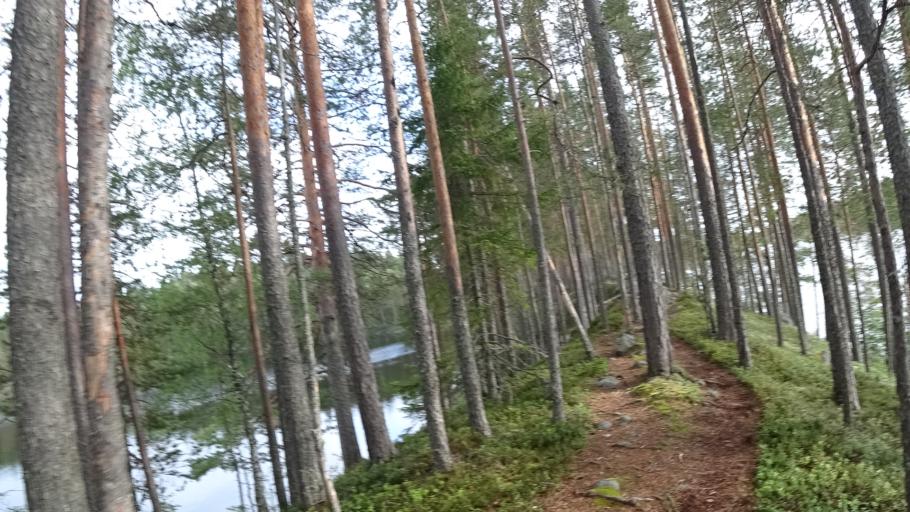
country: FI
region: North Karelia
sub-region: Joensuu
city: Ilomantsi
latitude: 62.5745
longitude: 31.1724
